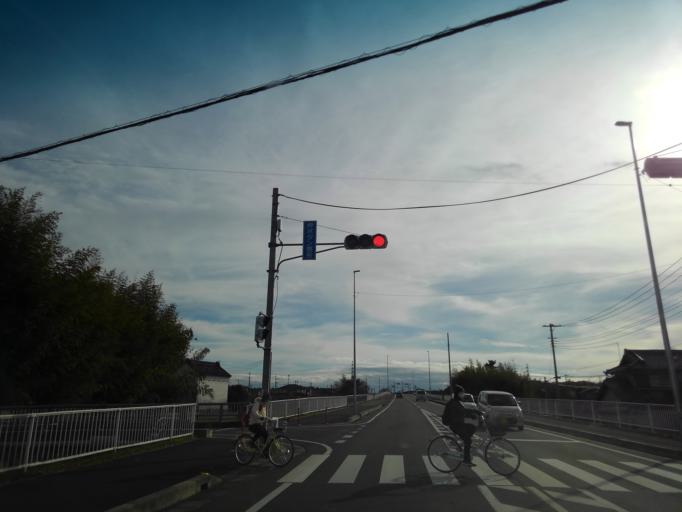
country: JP
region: Saitama
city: Morohongo
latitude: 35.9372
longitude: 139.3173
